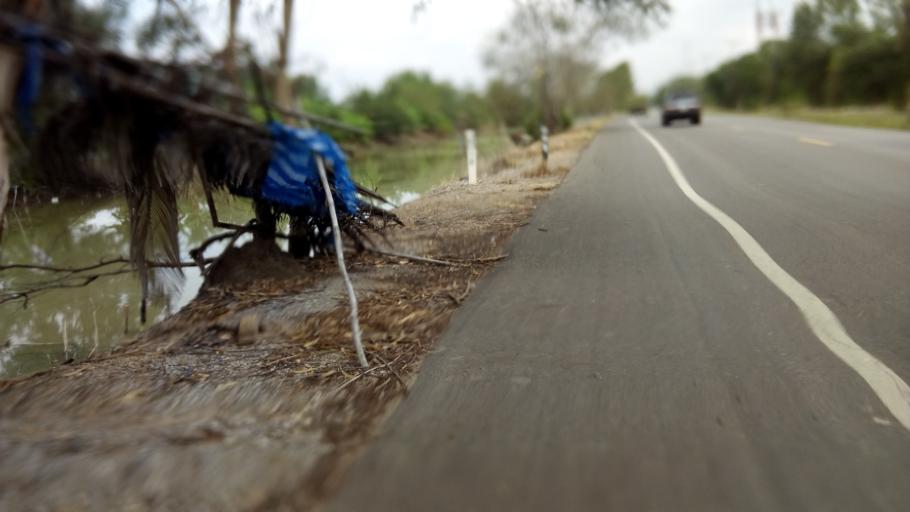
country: TH
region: Pathum Thani
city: Nong Suea
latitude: 14.2187
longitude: 100.8233
